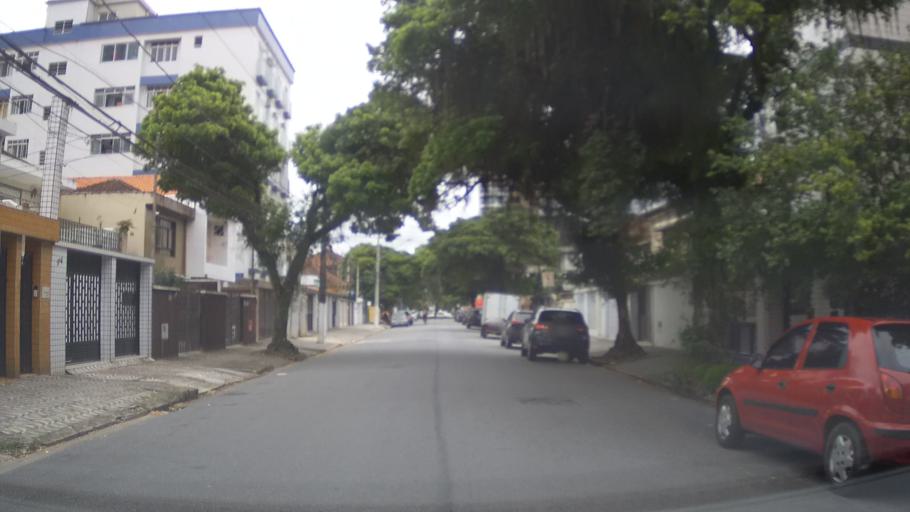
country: BR
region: Sao Paulo
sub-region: Santos
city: Santos
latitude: -23.9633
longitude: -46.3168
